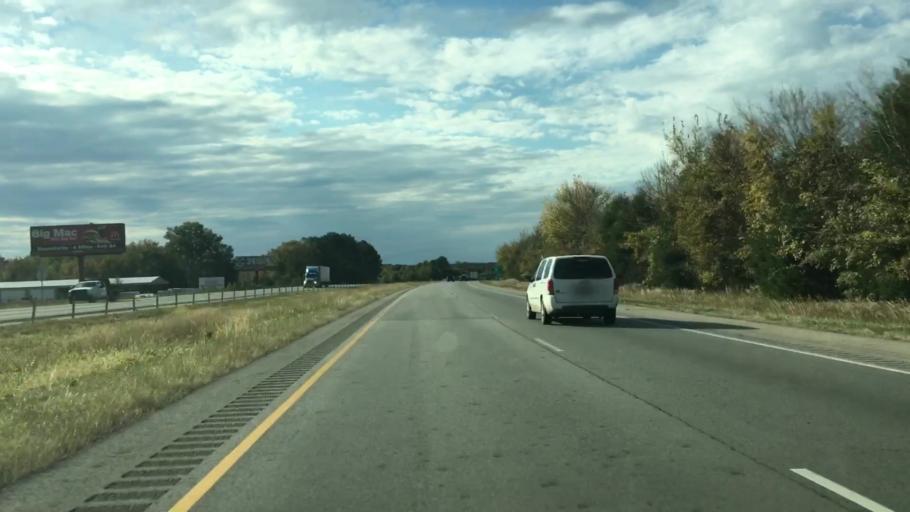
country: US
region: Arkansas
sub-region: Pope County
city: Pottsville
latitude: 35.2484
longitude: -93.0278
